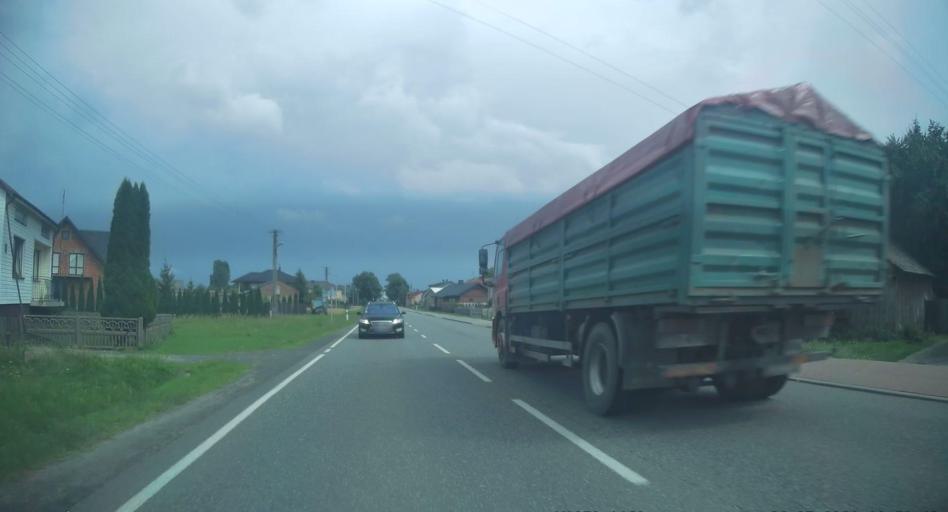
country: PL
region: Lodz Voivodeship
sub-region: Powiat skierniewicki
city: Gluchow
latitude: 51.7725
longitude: 20.1401
